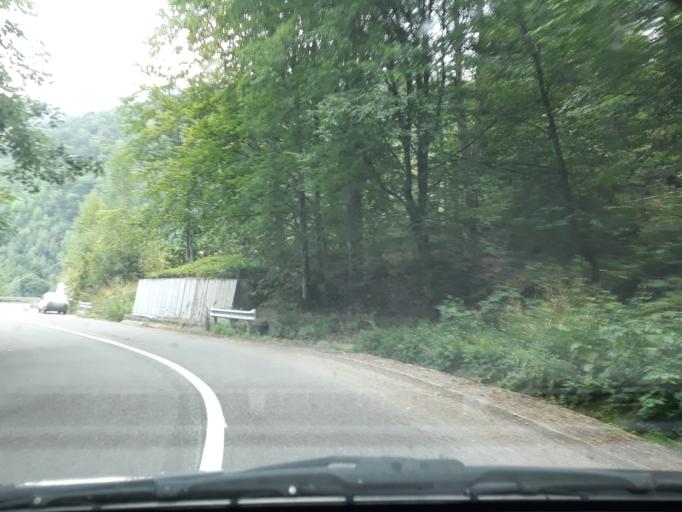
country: RO
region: Bihor
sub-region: Comuna Pietroasa
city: Pietroasa
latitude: 46.5983
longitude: 22.6547
